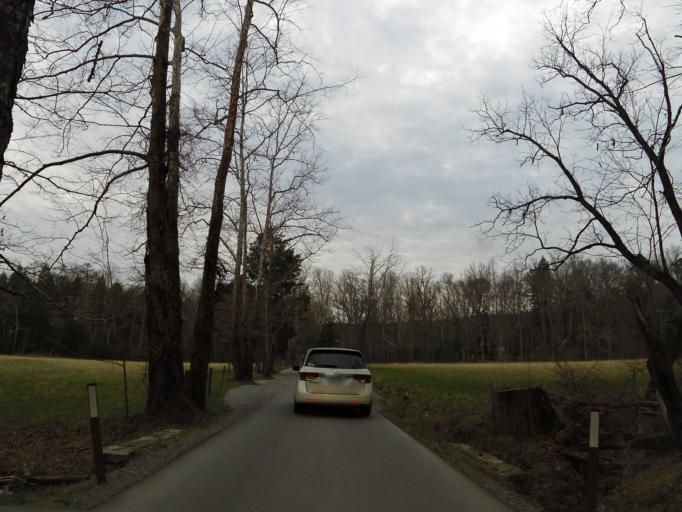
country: US
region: Tennessee
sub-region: Blount County
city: Wildwood
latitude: 35.6066
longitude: -83.8147
